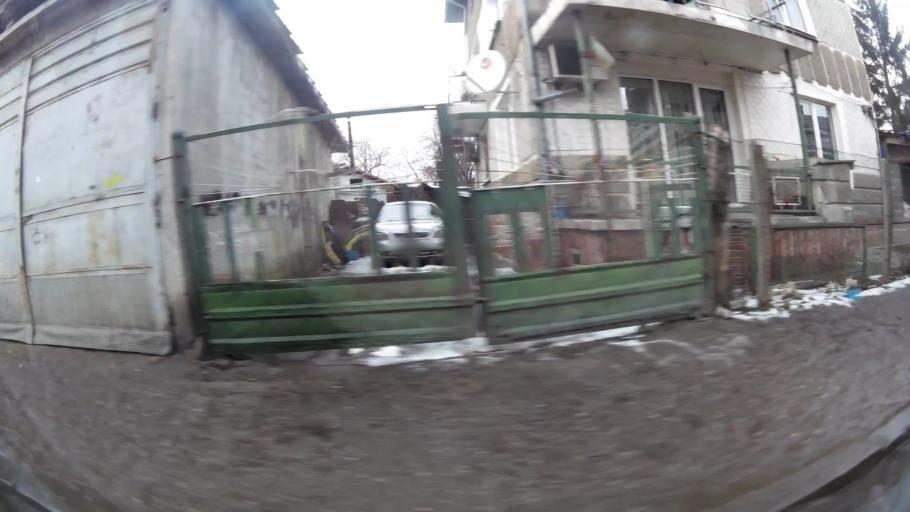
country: BG
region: Sofia-Capital
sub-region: Stolichna Obshtina
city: Sofia
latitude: 42.6896
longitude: 23.3807
